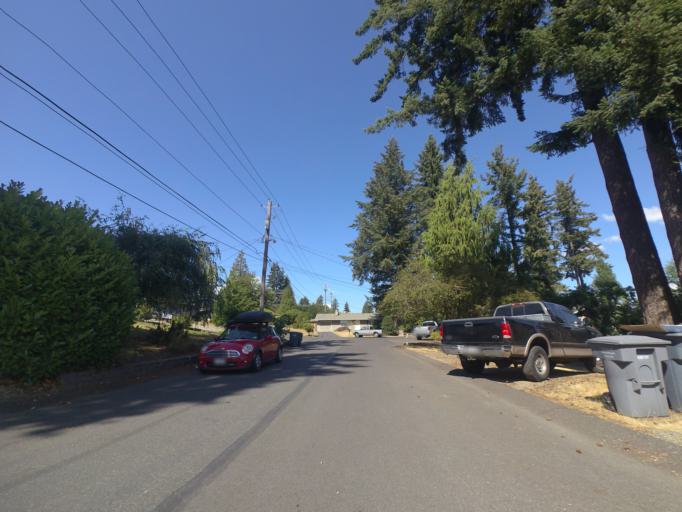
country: US
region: Washington
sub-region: Pierce County
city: Fircrest
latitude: 47.2201
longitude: -122.5123
